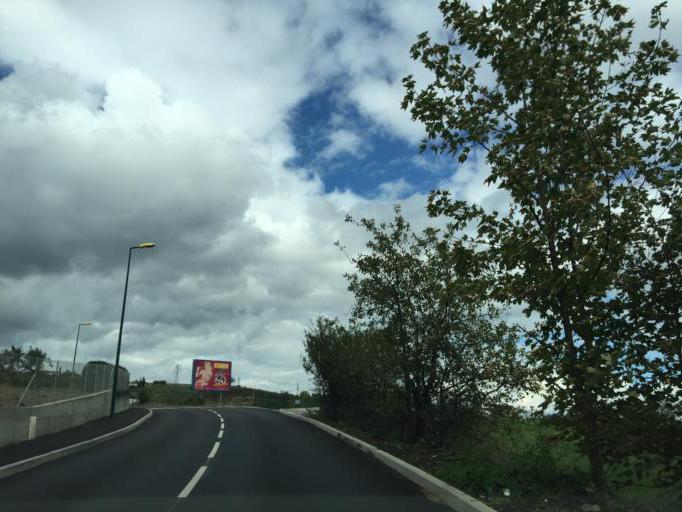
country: FR
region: Rhone-Alpes
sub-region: Departement de la Loire
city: Saint-Martin-la-Plaine
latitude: 45.5326
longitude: 4.5955
